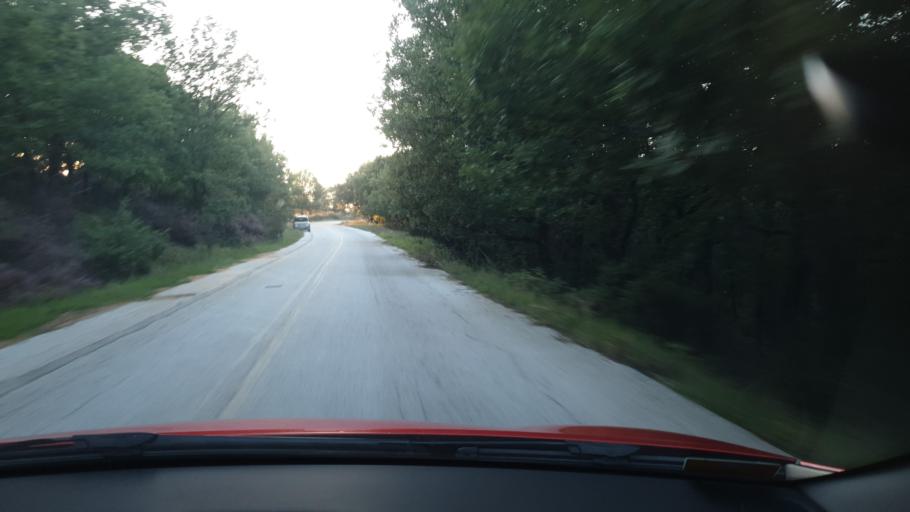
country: GR
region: Central Macedonia
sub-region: Nomos Thessalonikis
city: Peristera
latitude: 40.5170
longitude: 23.2121
